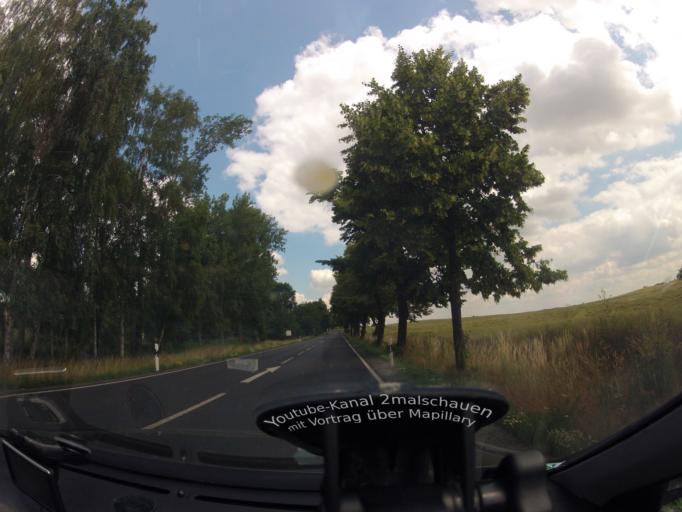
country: DE
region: Saxony
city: Jesewitz
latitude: 51.4093
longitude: 12.5403
